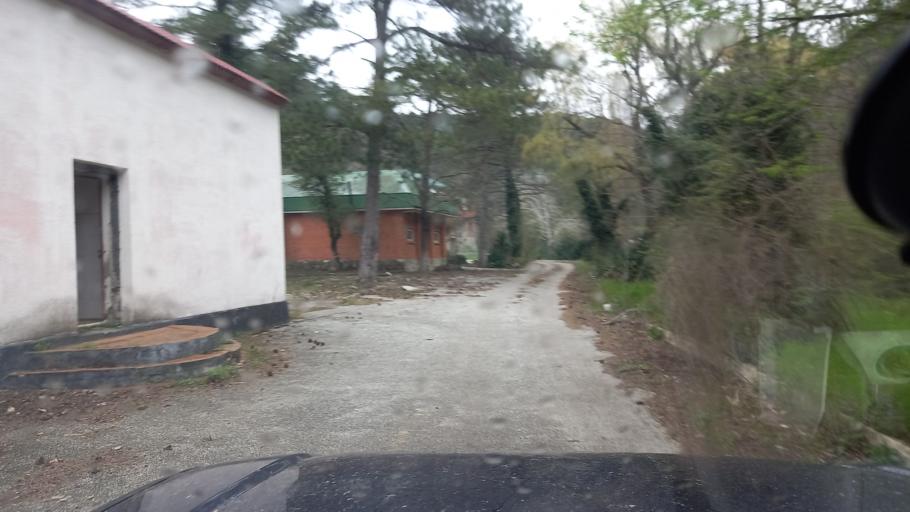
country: RU
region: Krasnodarskiy
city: Arkhipo-Osipovka
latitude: 44.3723
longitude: 38.4509
